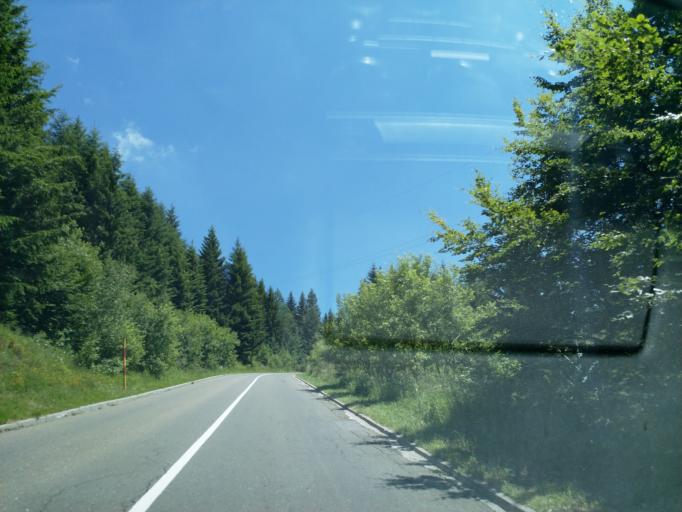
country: XK
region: Mitrovica
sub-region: Komuna e Leposaviqit
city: Leposaviq
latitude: 43.2744
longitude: 20.7870
